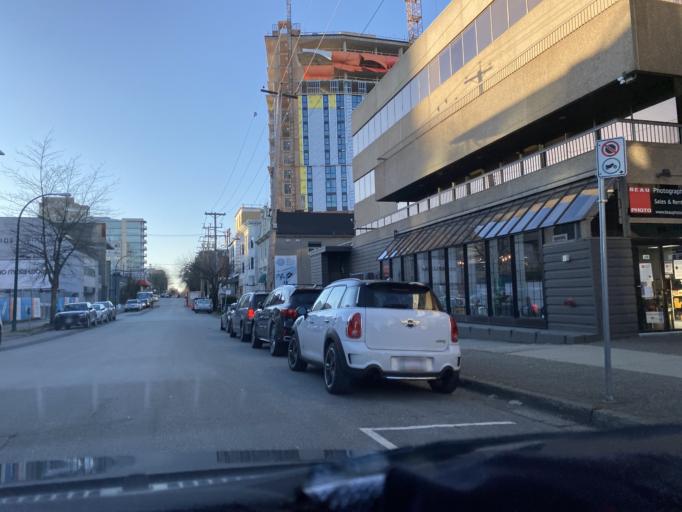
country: CA
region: British Columbia
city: West End
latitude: 49.2645
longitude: -123.1362
